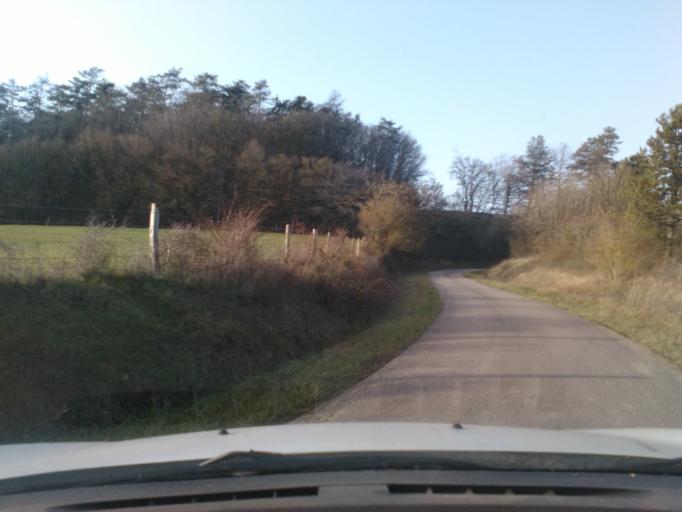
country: FR
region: Lorraine
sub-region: Departement des Vosges
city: Vittel
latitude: 48.2557
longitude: 6.0015
